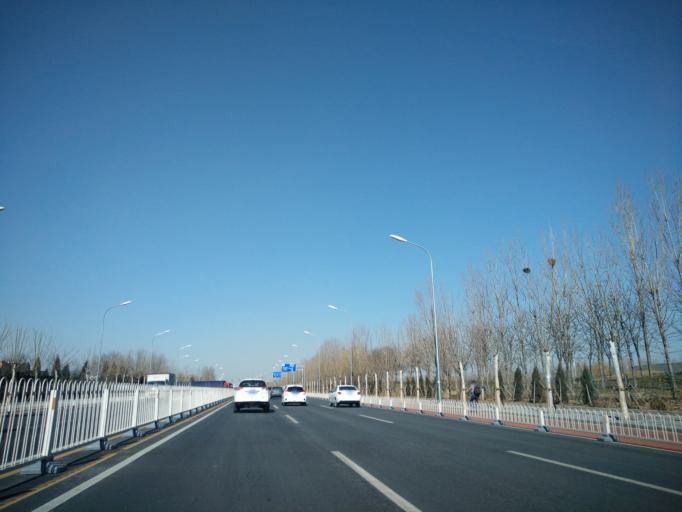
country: CN
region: Beijing
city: Jiugong
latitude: 39.7765
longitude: 116.5393
